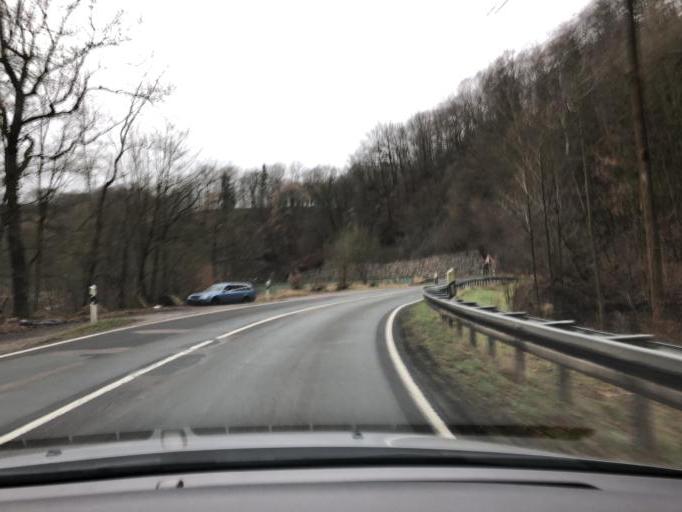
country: DE
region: Saxony
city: Niederstriegis
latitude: 51.0906
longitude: 13.1356
